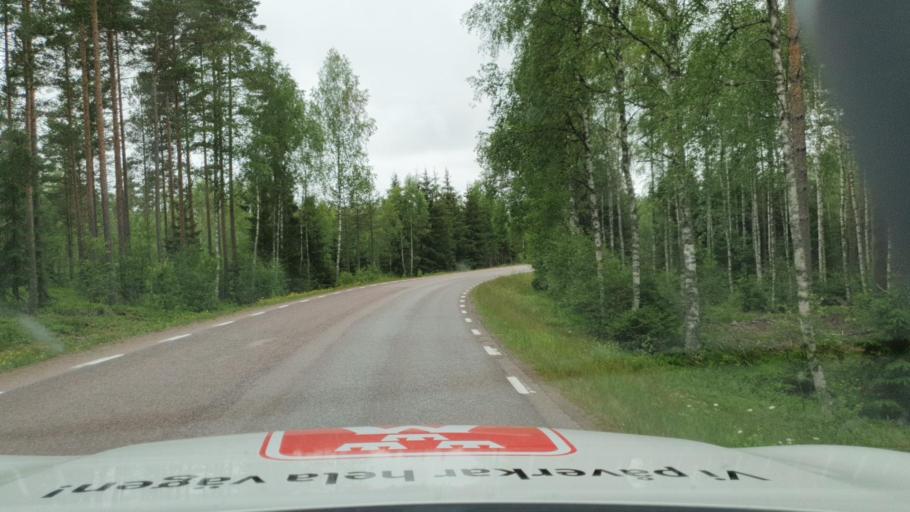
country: SE
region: Vaermland
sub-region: Kristinehamns Kommun
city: Kristinehamn
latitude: 59.4704
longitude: 13.9370
